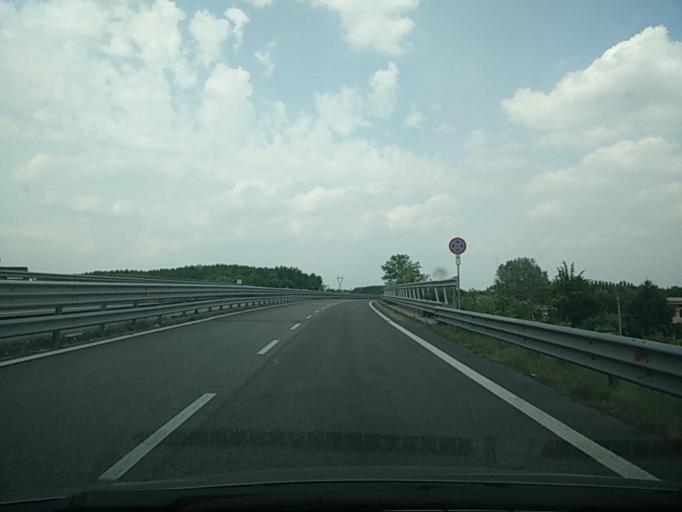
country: IT
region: Friuli Venezia Giulia
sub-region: Provincia di Pordenone
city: Fiume Veneto
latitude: 45.9333
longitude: 12.7141
